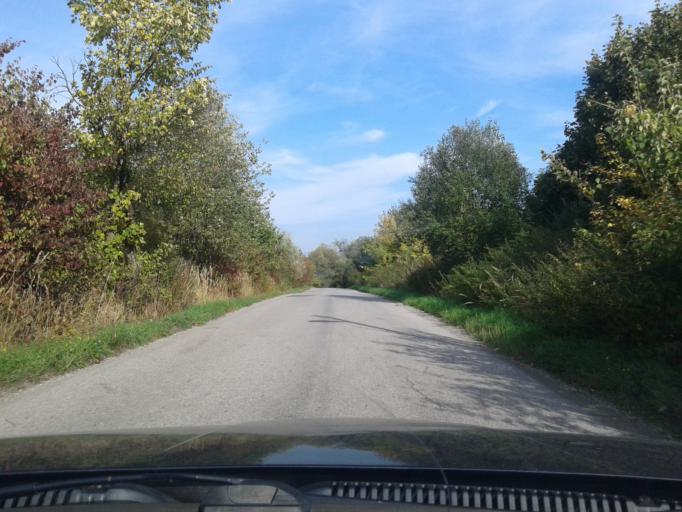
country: CZ
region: Moravskoslezsky
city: Orlova
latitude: 49.8548
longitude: 18.4509
